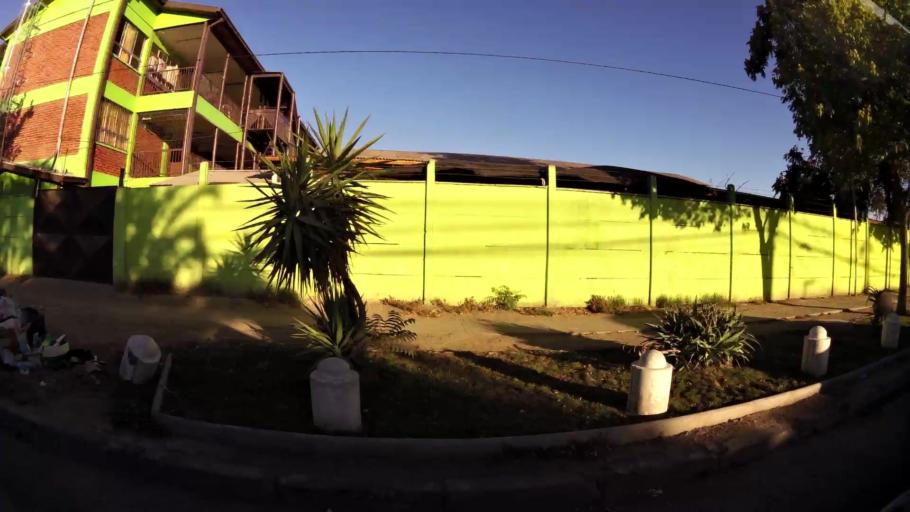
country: CL
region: O'Higgins
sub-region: Provincia de Cachapoal
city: Rancagua
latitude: -34.1676
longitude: -70.7595
